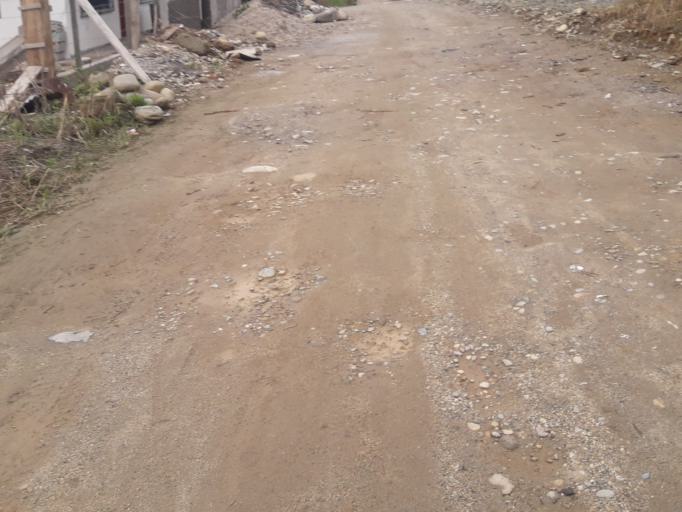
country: EC
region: Napo
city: Tena
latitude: -0.9851
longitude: -77.8276
